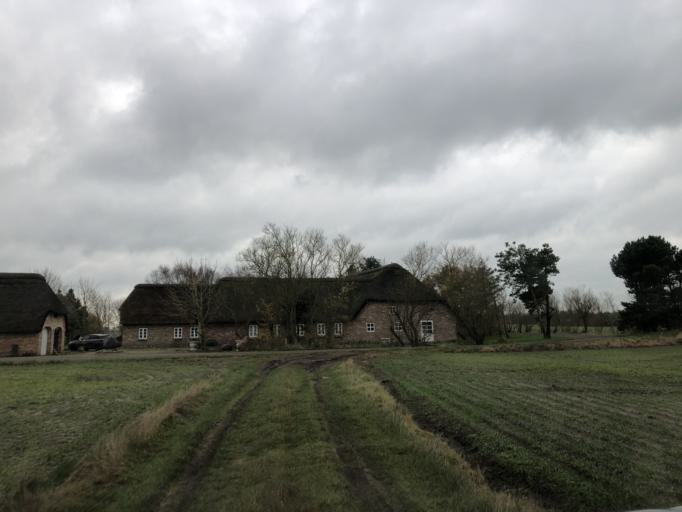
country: DK
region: Central Jutland
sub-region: Holstebro Kommune
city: Ulfborg
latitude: 56.3120
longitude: 8.2046
